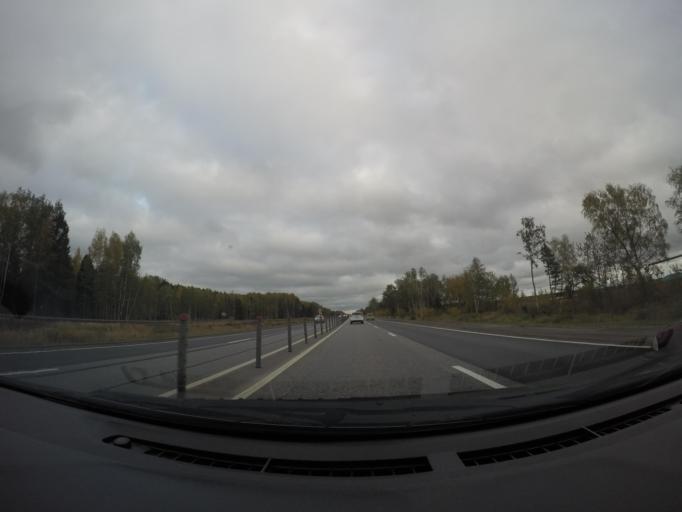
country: RU
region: Moskovskaya
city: Chupryakovo
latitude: 55.5590
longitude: 36.5838
